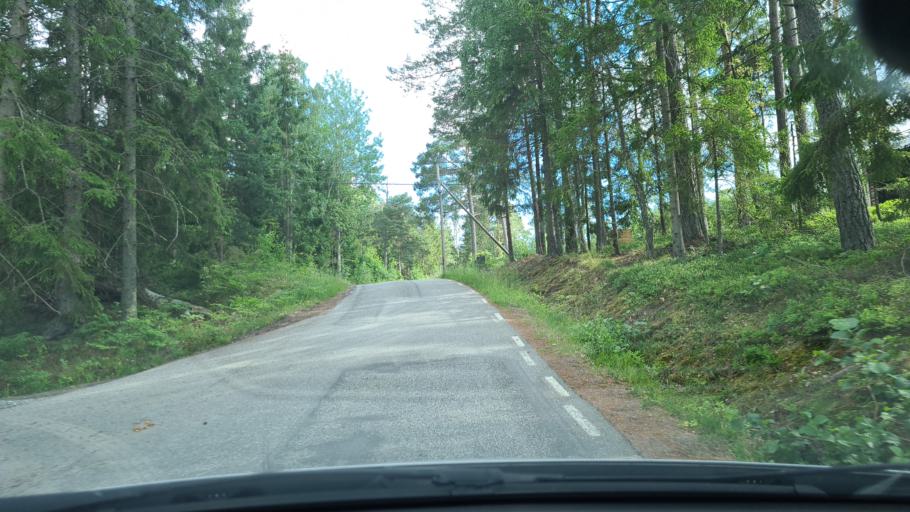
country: SE
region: Stockholm
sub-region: Vaxholms Kommun
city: Vaxholm
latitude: 59.4201
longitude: 18.4324
